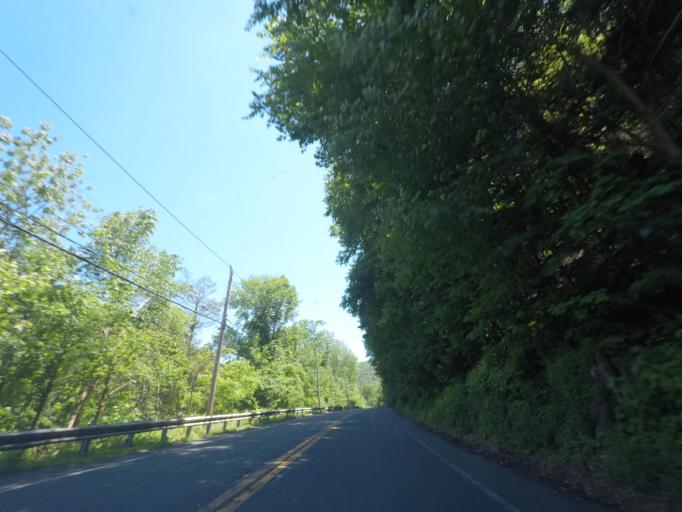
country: US
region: Massachusetts
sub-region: Berkshire County
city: Becket
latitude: 42.2605
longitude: -72.9580
